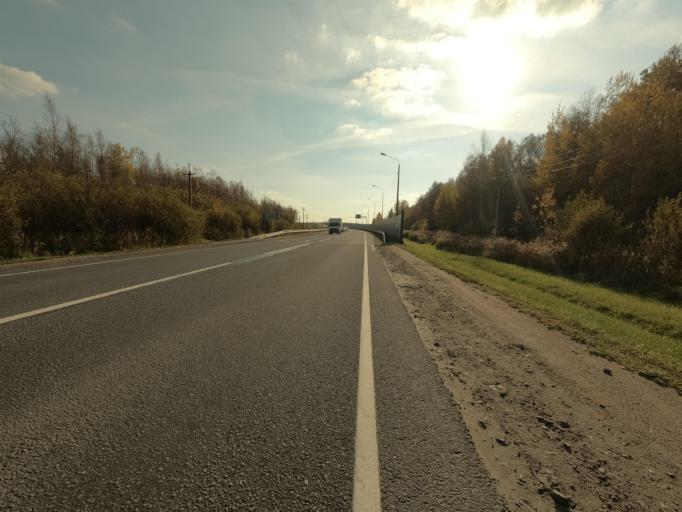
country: RU
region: Leningrad
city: Mga
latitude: 59.7630
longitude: 31.0945
